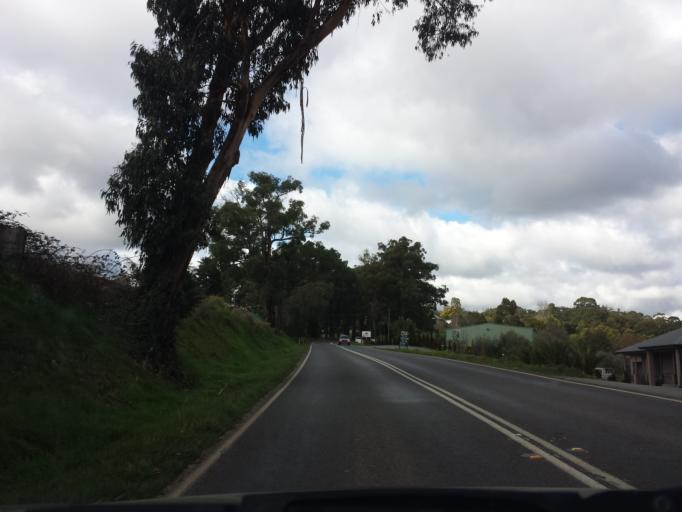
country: AU
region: Victoria
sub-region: Yarra Ranges
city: Mount Evelyn
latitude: -37.8127
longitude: 145.4062
